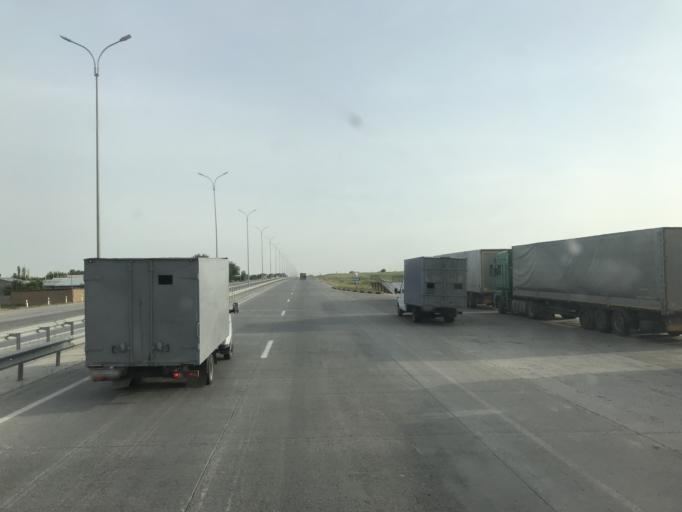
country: UZ
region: Toshkent
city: Qibray
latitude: 41.5558
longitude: 69.4077
